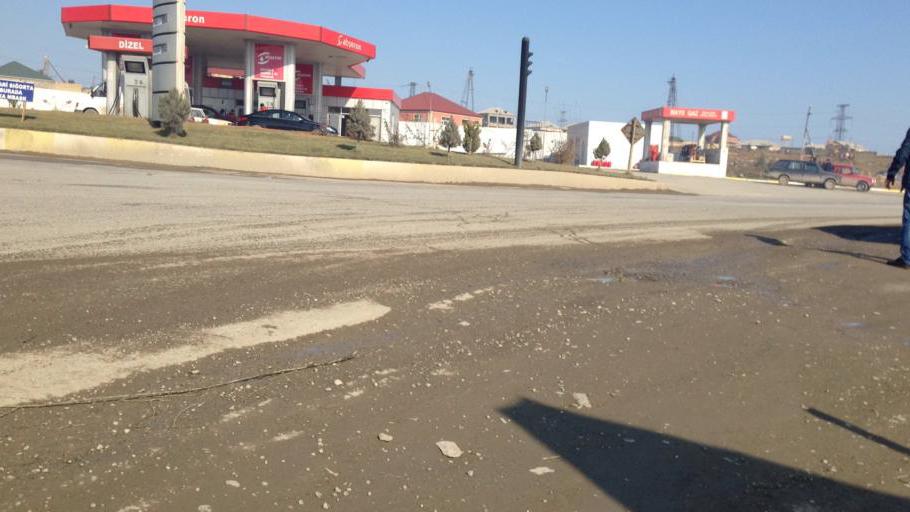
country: AZ
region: Abseron
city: Digah
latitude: 40.4803
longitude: 49.8558
